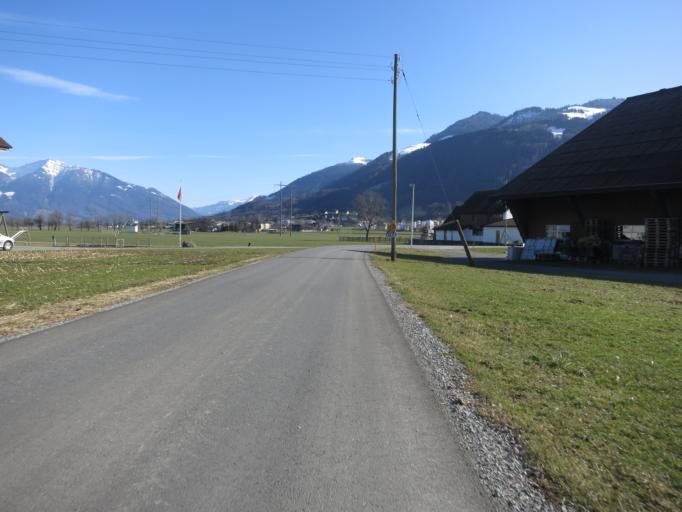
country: CH
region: Schwyz
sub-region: Bezirk March
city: Schubelbach
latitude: 47.1799
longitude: 8.9272
